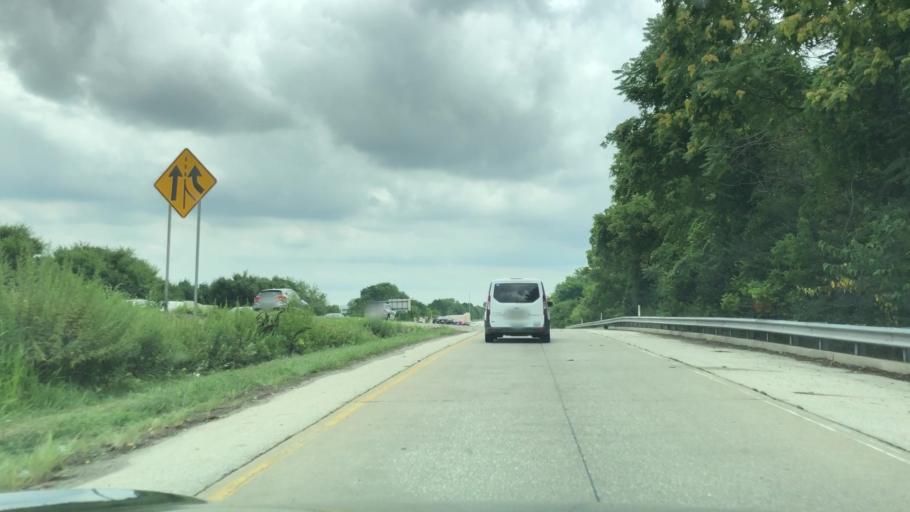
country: US
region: Pennsylvania
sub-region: Chester County
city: Devon
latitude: 40.0735
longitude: -75.4258
